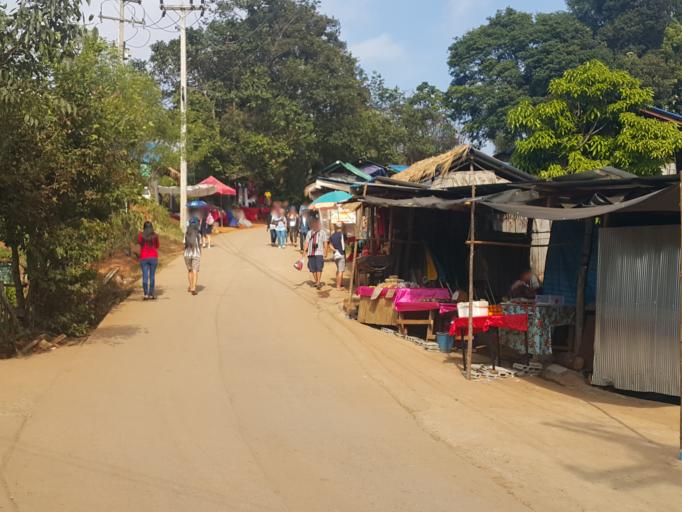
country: TH
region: Chiang Mai
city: Samoeng
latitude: 18.9348
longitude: 98.8228
